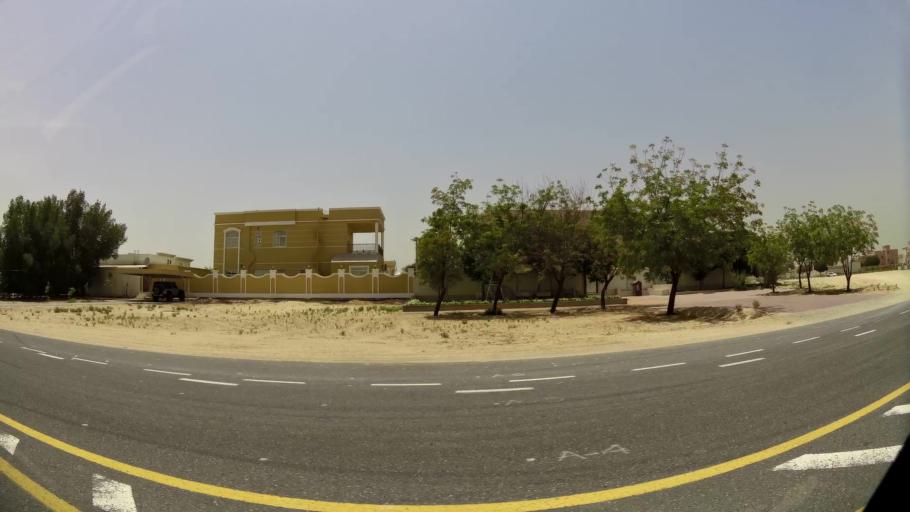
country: AE
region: Ash Shariqah
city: Sharjah
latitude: 25.1985
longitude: 55.3915
